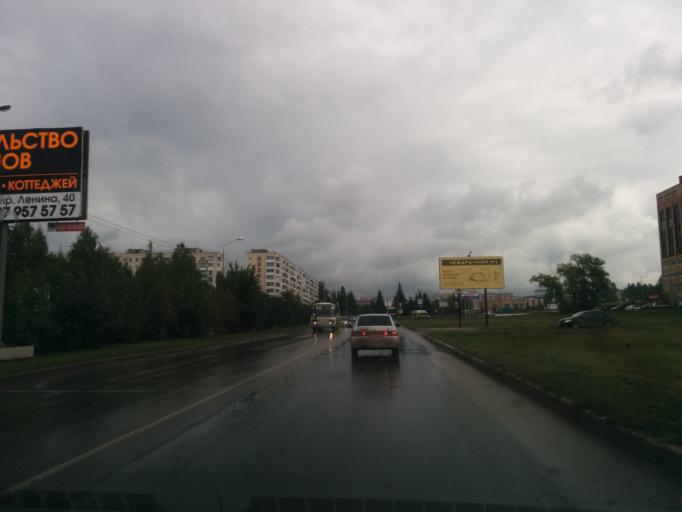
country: RU
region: Bashkortostan
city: Oktyabr'skiy
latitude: 54.4838
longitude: 53.4948
